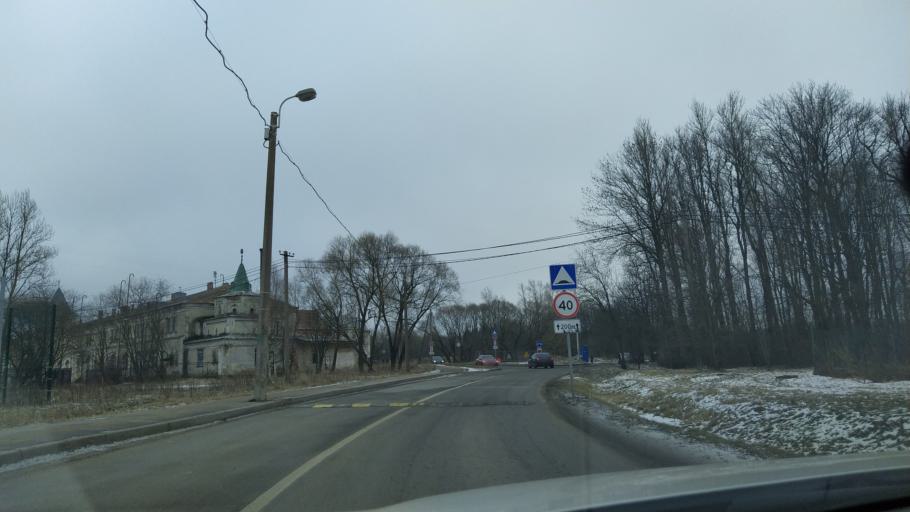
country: RU
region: St.-Petersburg
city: Pushkin
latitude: 59.7303
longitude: 30.3852
